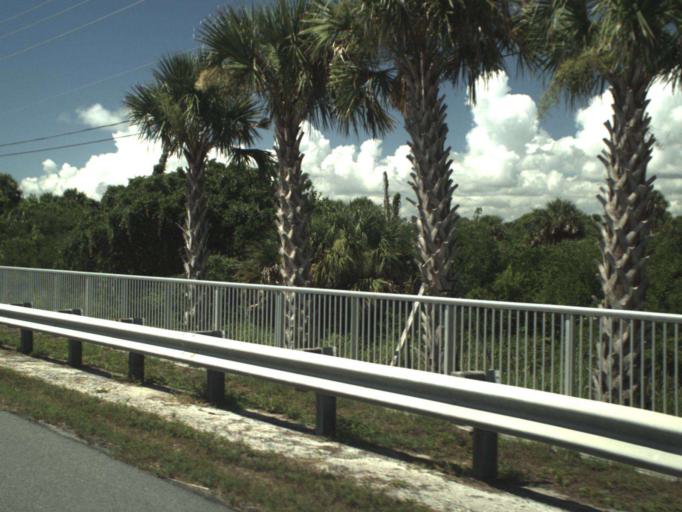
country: US
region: Florida
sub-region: Indian River County
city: South Beach
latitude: 27.5445
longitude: -80.3187
